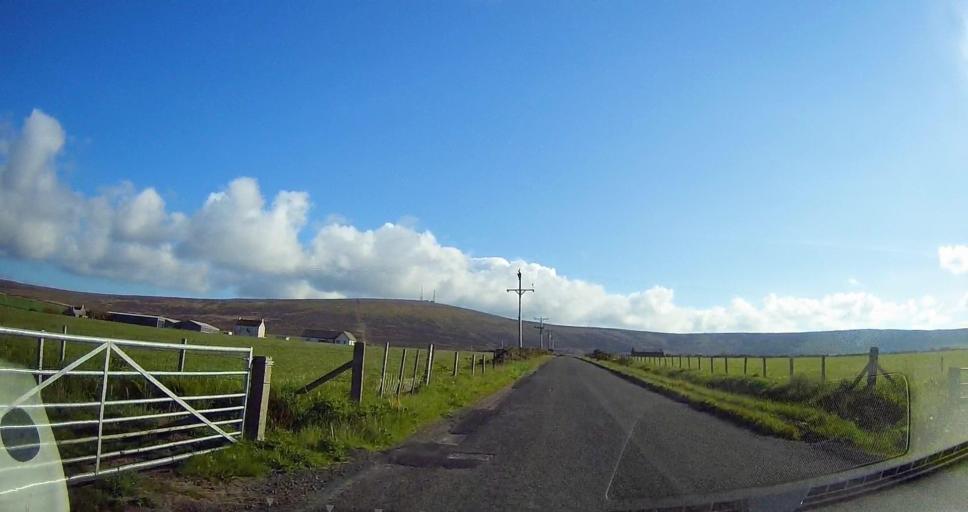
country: GB
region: Scotland
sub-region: Orkney Islands
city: Orkney
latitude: 58.9939
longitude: -3.0710
